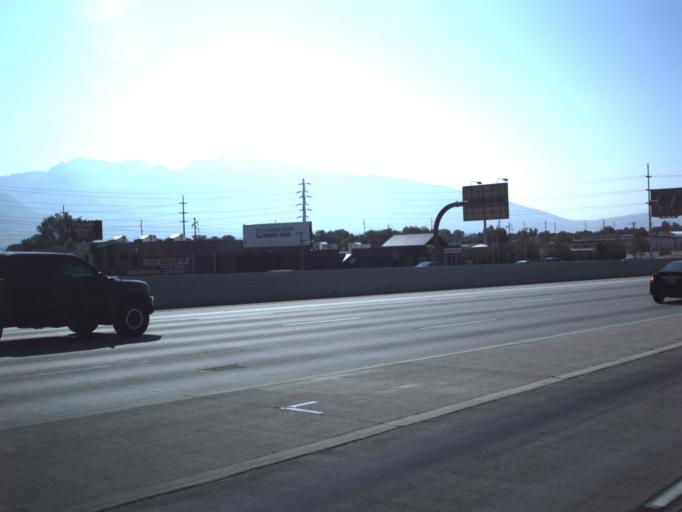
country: US
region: Utah
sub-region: Salt Lake County
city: Murray
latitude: 40.6493
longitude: -111.9027
